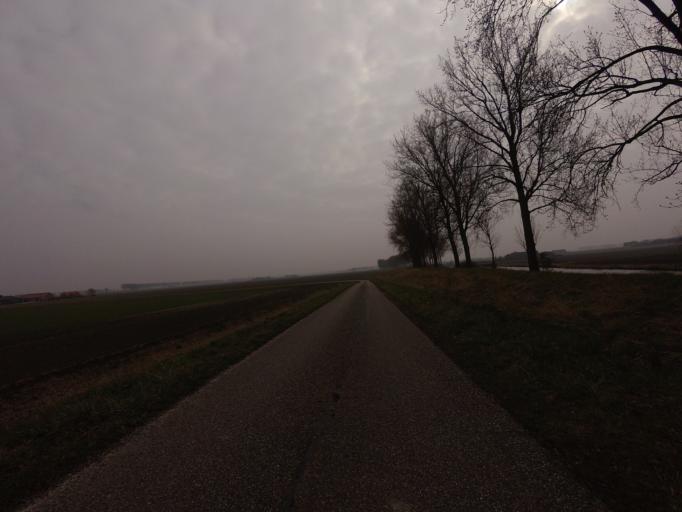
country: NL
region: Zeeland
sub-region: Gemeente Hulst
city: Hulst
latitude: 51.3459
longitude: 4.1082
